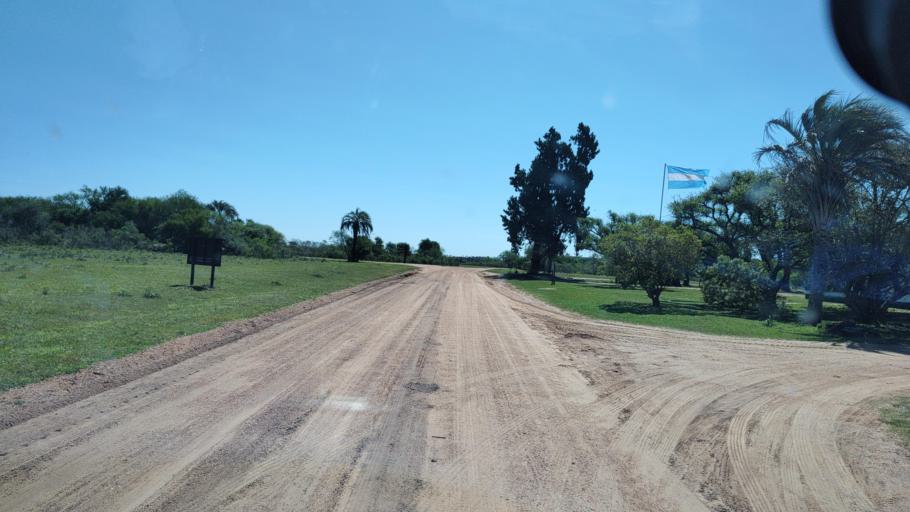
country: AR
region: Entre Rios
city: Ubajay
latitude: -31.8652
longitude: -58.2590
